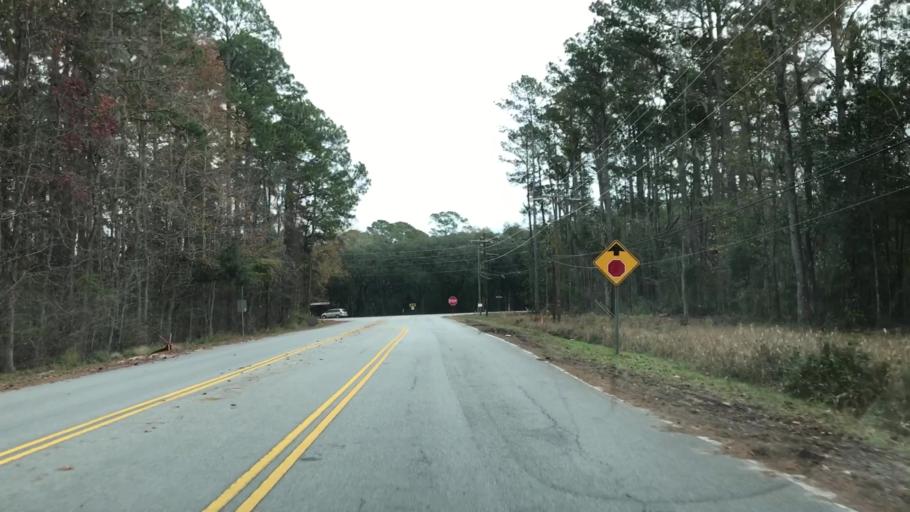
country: US
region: South Carolina
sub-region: Beaufort County
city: Burton
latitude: 32.4187
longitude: -80.7322
